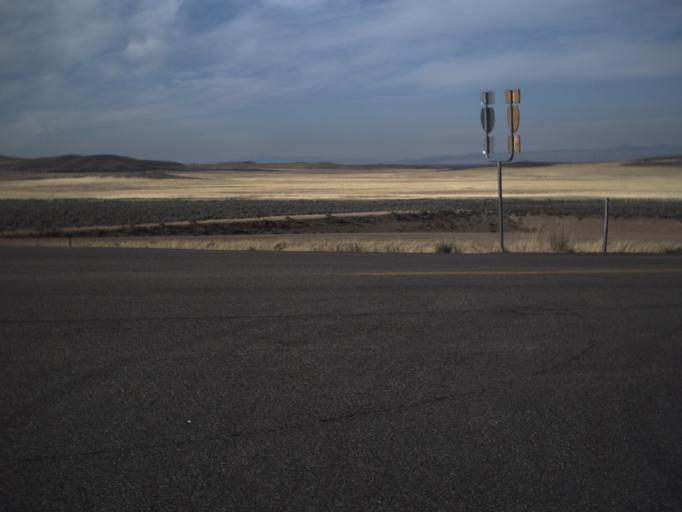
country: US
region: Utah
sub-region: Millard County
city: Fillmore
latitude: 39.0832
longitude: -112.2776
